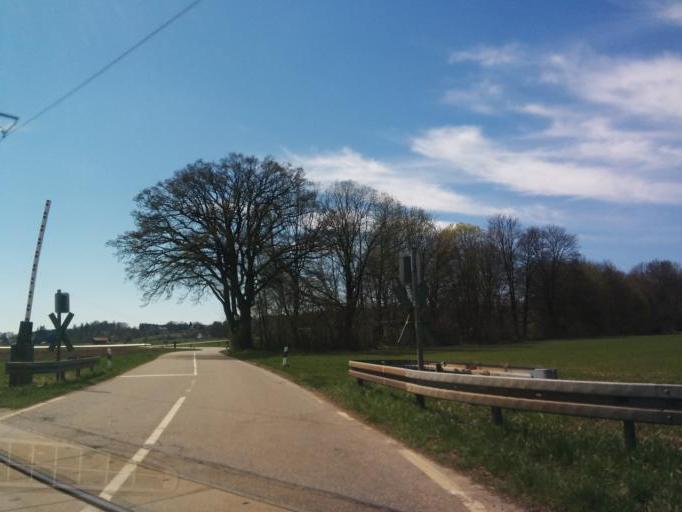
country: DE
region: Bavaria
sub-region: Upper Bavaria
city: Schaftlarn
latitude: 47.9723
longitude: 11.4479
